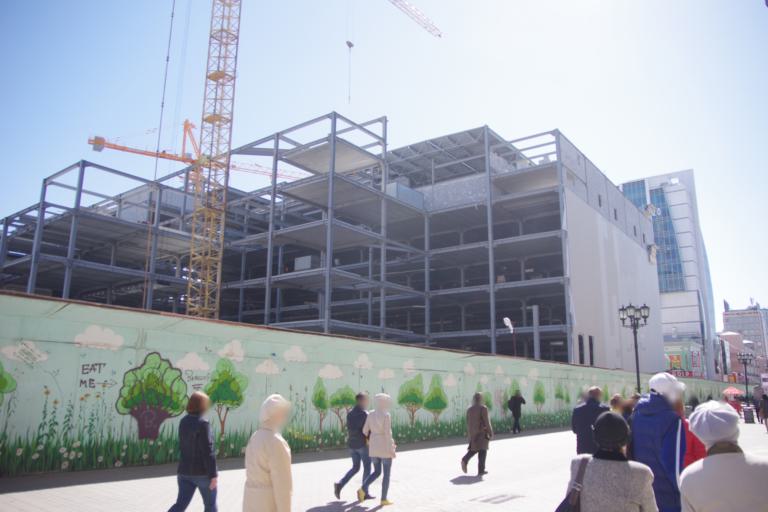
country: RU
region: Sverdlovsk
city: Yekaterinburg
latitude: 56.8370
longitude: 60.5946
